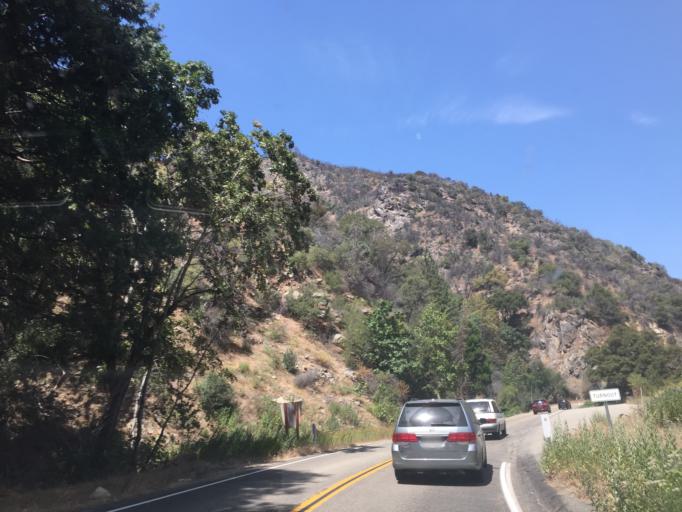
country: US
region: California
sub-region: Tulare County
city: Three Rivers
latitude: 36.8131
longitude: -118.8347
